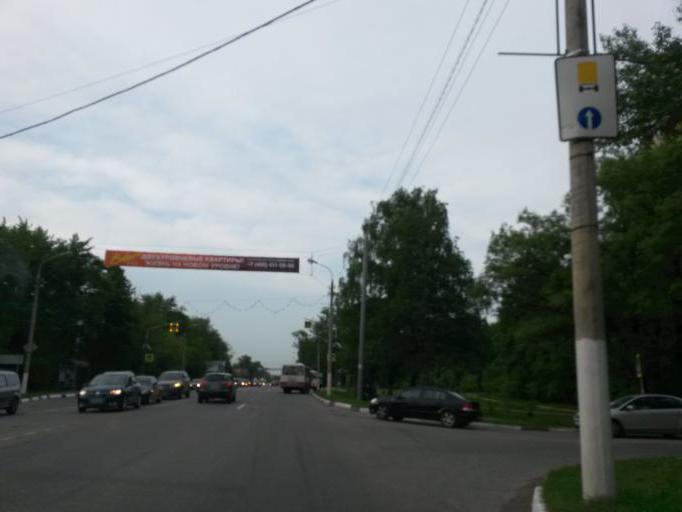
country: RU
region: Moskovskaya
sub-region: Chekhovskiy Rayon
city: Chekhov
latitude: 55.1501
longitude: 37.4584
